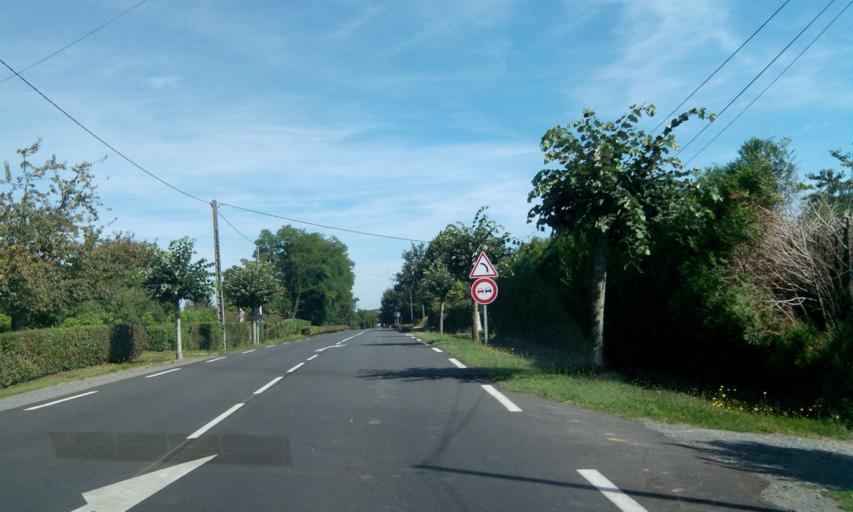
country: FR
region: Poitou-Charentes
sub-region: Departement de la Charente
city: Confolens
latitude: 45.9607
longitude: 0.7014
